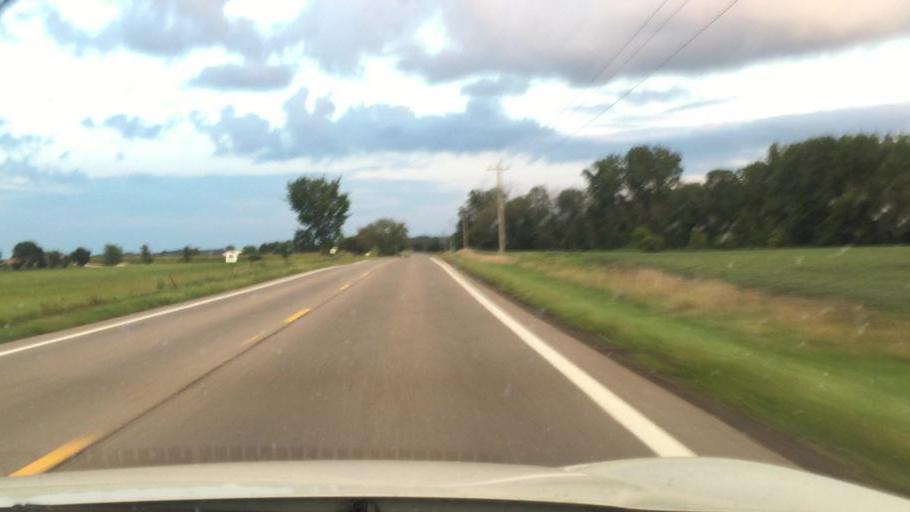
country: US
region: Ohio
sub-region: Champaign County
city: Mechanicsburg
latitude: 40.0516
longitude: -83.5255
